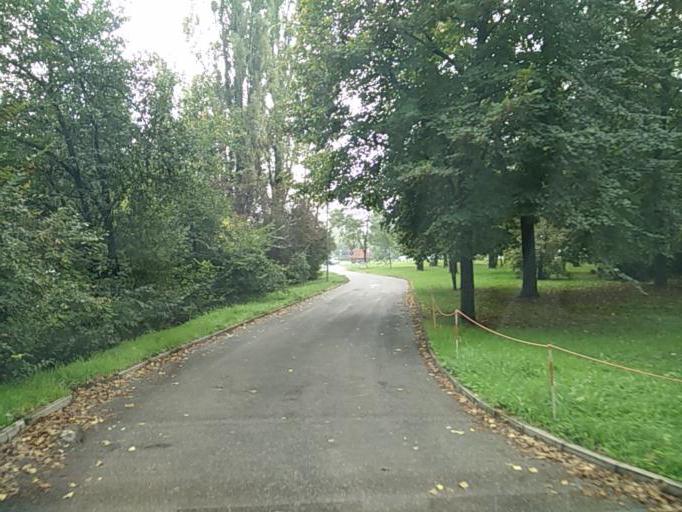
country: IT
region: Emilia-Romagna
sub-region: Provincia di Modena
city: Carpi Centro
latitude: 44.7824
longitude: 10.8675
